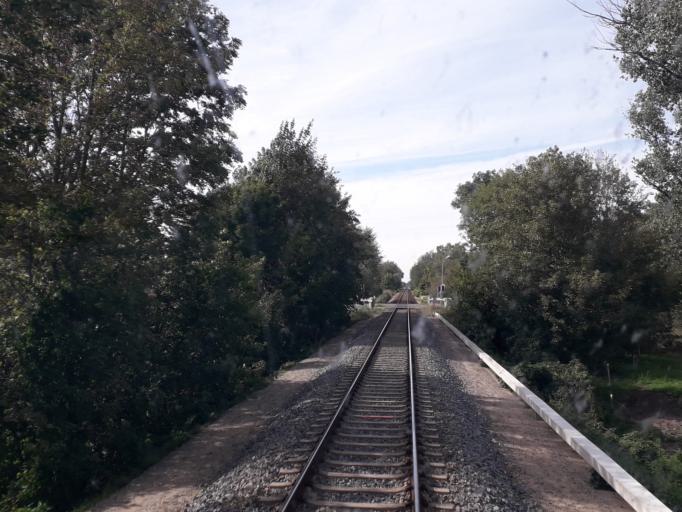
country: DE
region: Brandenburg
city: Kremmen
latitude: 52.7381
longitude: 13.0825
